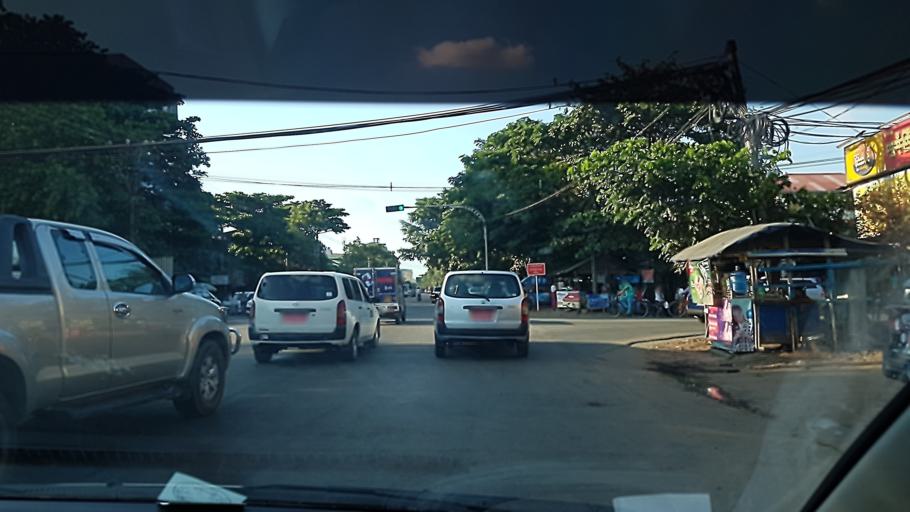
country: MM
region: Yangon
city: Yangon
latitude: 16.8416
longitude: 96.1832
